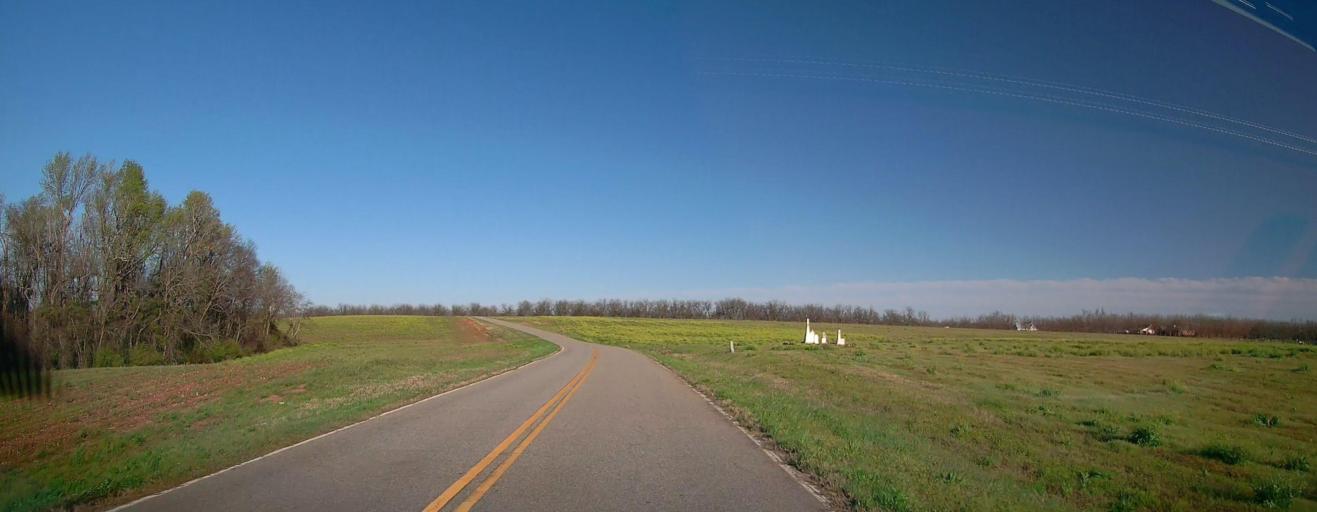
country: US
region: Georgia
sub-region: Houston County
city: Perry
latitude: 32.3677
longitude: -83.6939
